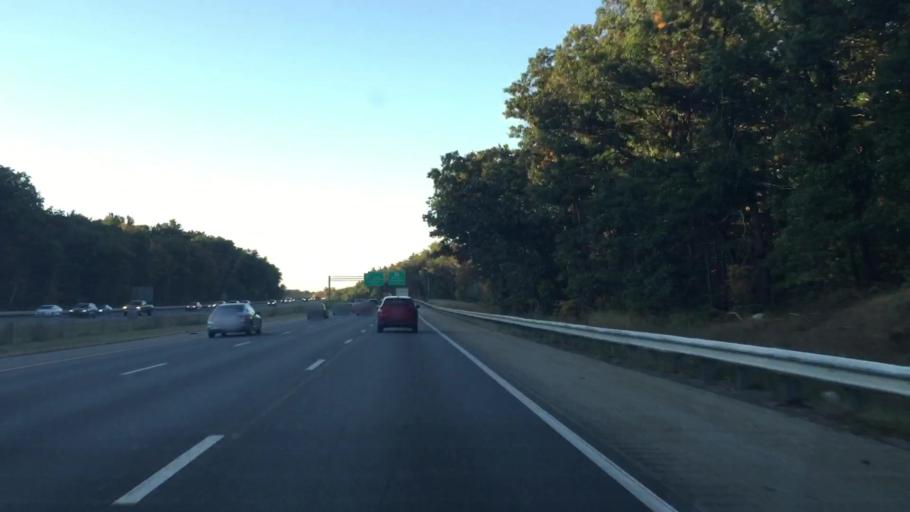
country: US
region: Massachusetts
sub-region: Middlesex County
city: Billerica
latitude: 42.5802
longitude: -71.3074
